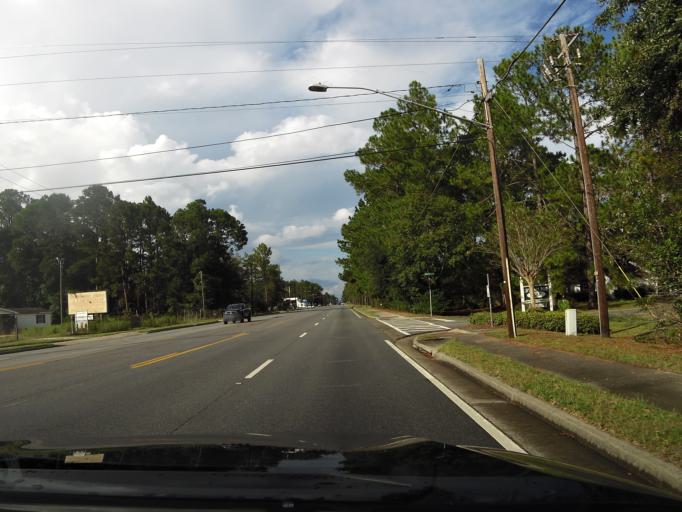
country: US
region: Georgia
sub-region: Liberty County
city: Walthourville
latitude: 31.8011
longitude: -81.6054
